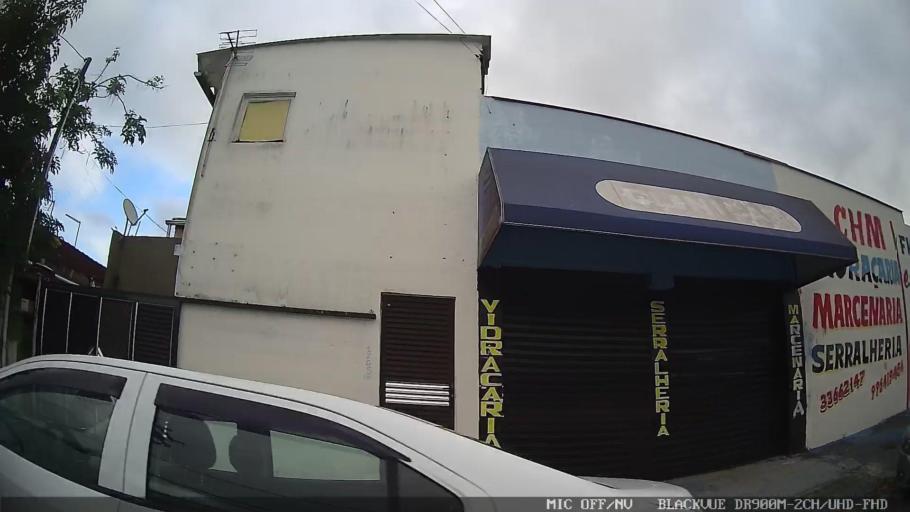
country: BR
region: Sao Paulo
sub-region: Peruibe
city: Peruibe
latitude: -24.3070
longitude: -46.9937
